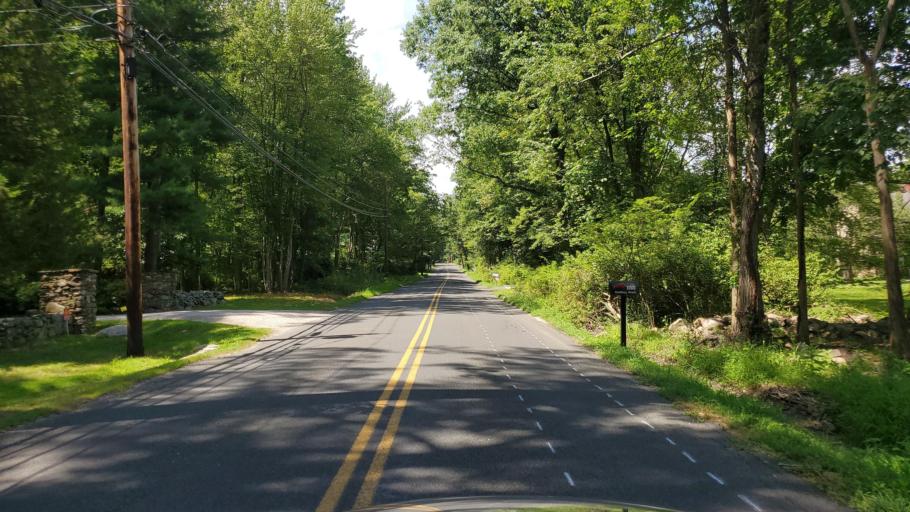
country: US
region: Connecticut
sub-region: Fairfield County
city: Southport
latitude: 41.1640
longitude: -73.2921
